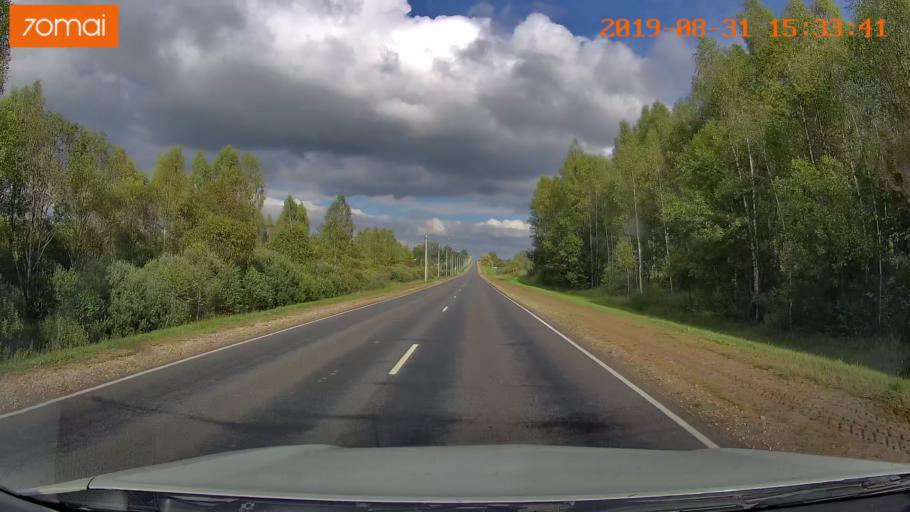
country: RU
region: Kaluga
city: Mosal'sk
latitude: 54.5966
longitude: 34.7058
